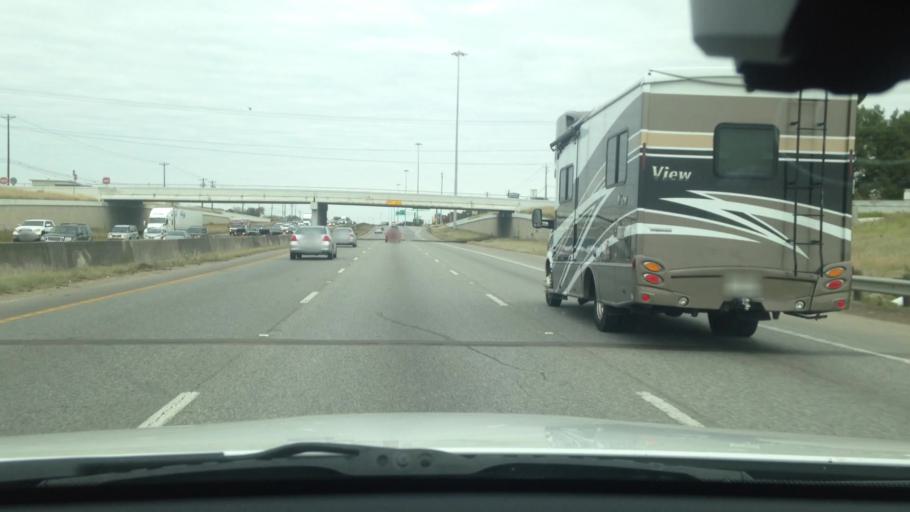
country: US
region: Texas
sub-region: Travis County
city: Onion Creek
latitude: 30.1357
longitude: -97.7976
